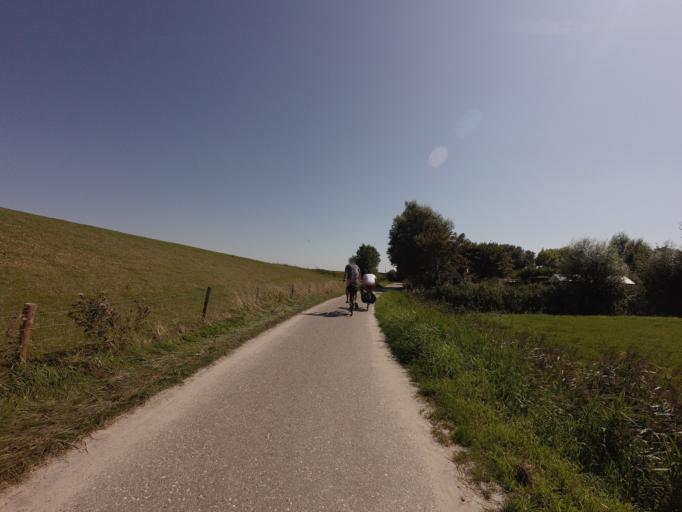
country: NL
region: Friesland
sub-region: Gemeente Dongeradeel
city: Anjum
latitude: 53.3977
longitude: 6.1040
